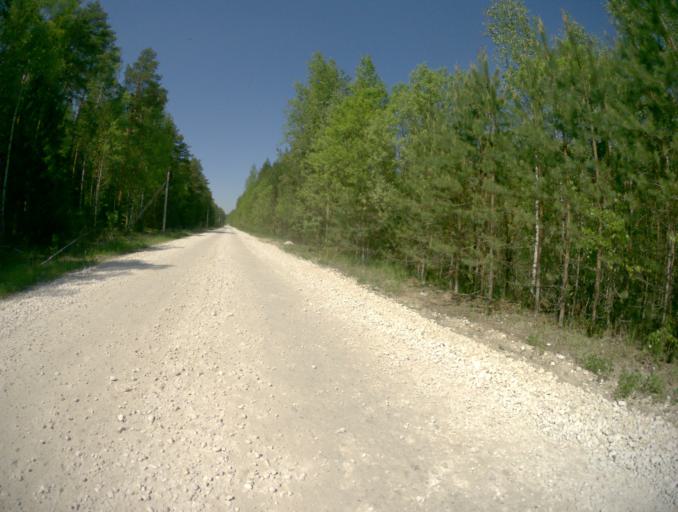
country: RU
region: Vladimir
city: Gusevskiy
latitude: 55.7207
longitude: 40.5877
